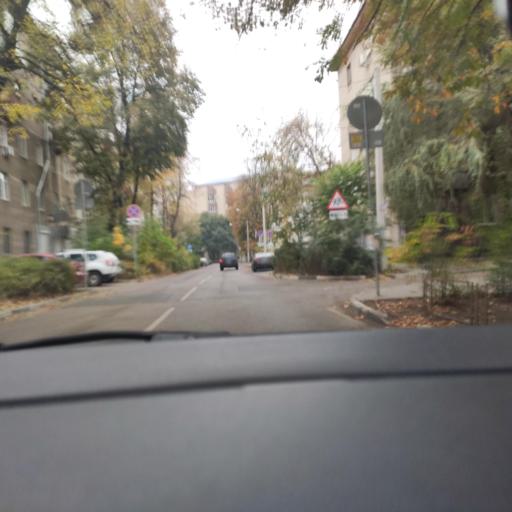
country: RU
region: Voronezj
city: Voronezh
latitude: 51.6724
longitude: 39.1986
